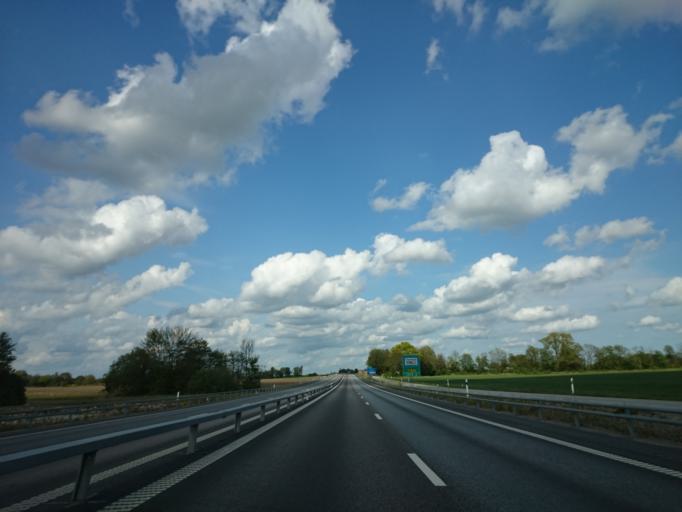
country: SE
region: Skane
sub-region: Hoors Kommun
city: Loberod
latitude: 55.8173
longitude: 13.5014
